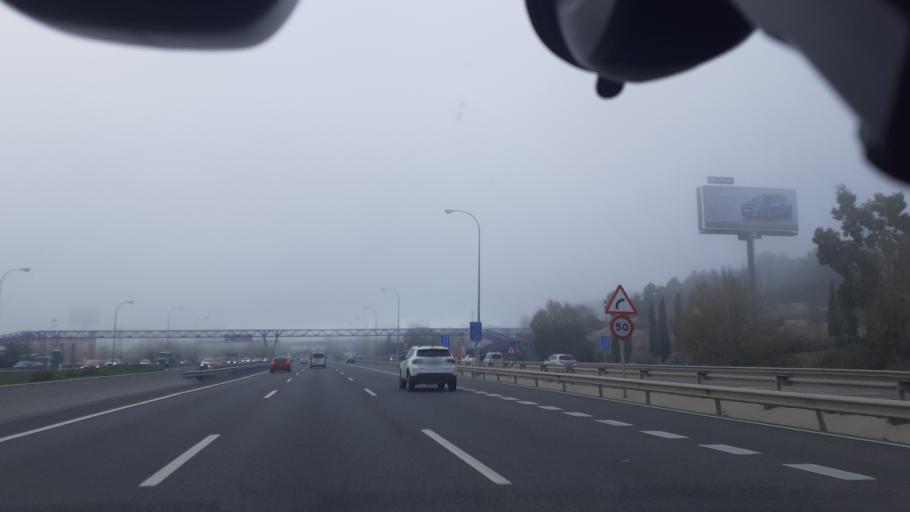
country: ES
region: Madrid
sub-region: Provincia de Madrid
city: Vicalvaro
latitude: 40.3911
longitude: -3.6227
